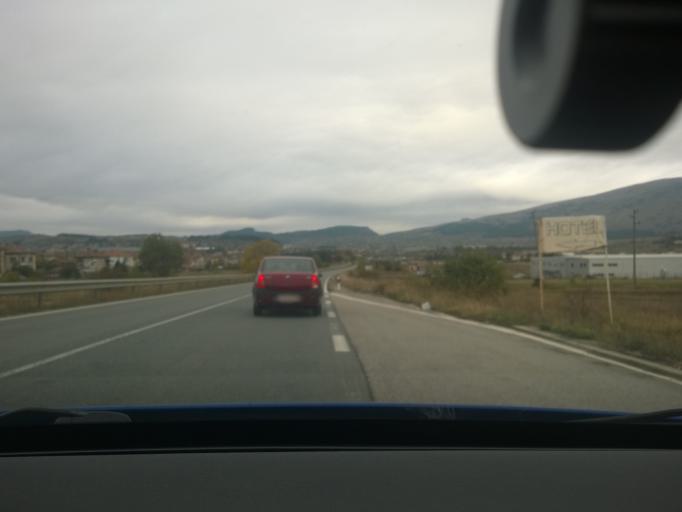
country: BG
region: Sofiya
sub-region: Obshtina Dragoman
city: Dragoman
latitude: 42.9139
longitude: 22.9410
